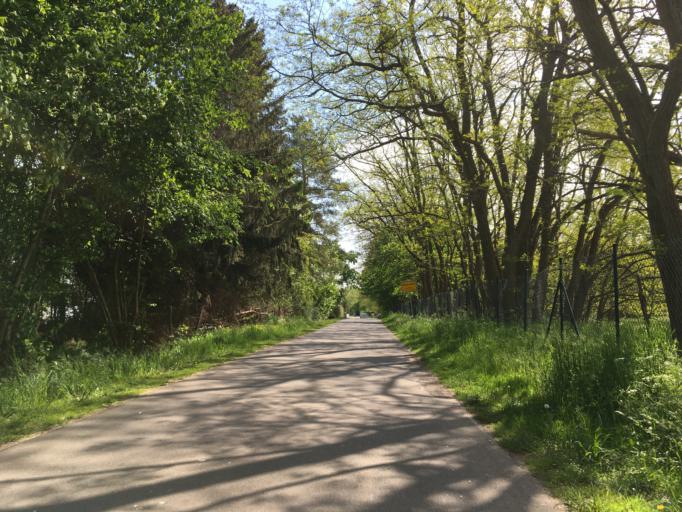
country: DE
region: Brandenburg
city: Werneuchen
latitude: 52.6005
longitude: 13.7433
